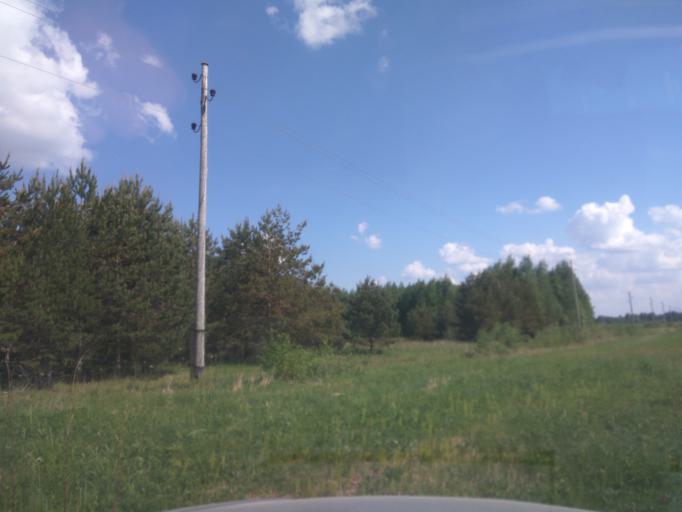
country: LV
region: Kuldigas Rajons
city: Kuldiga
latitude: 57.1800
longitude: 22.0044
